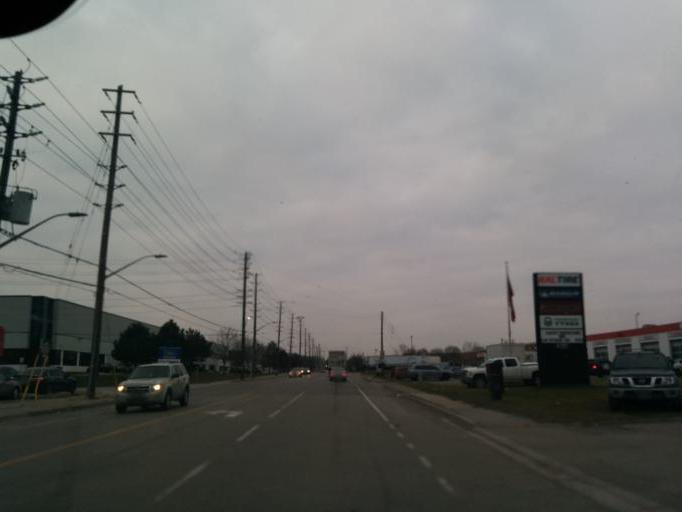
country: CA
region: Ontario
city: Etobicoke
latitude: 43.5990
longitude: -79.5839
